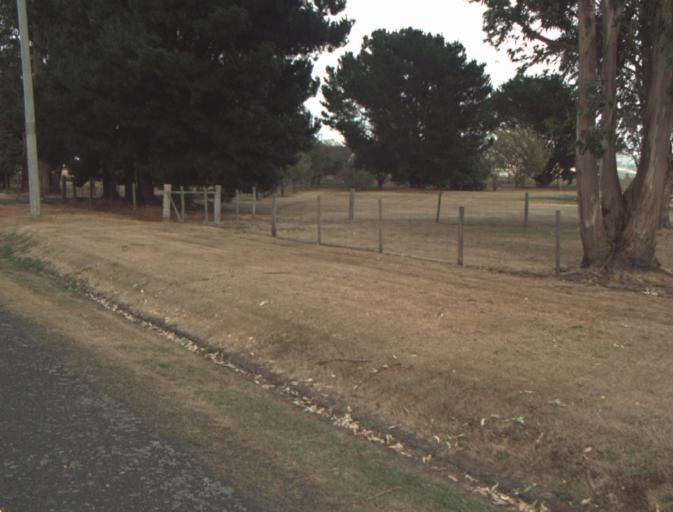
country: AU
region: Tasmania
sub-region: Launceston
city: Mayfield
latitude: -41.3319
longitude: 147.0549
